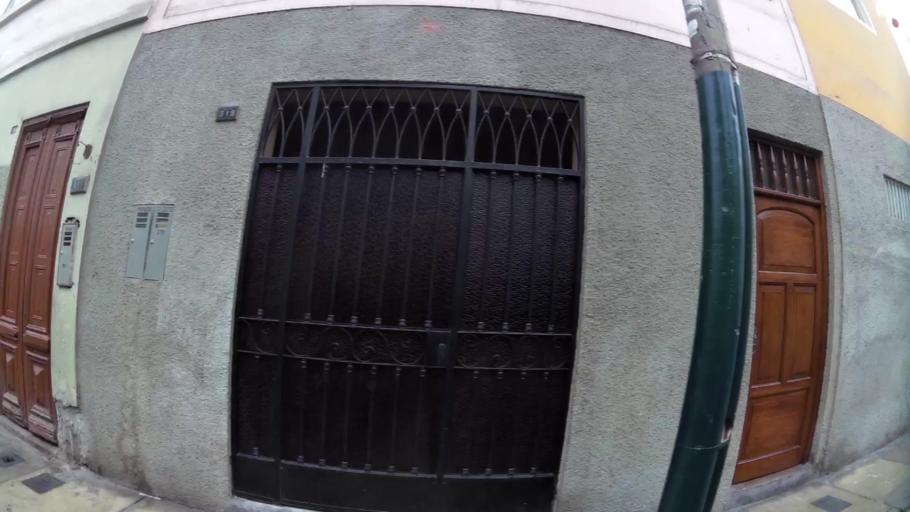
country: PE
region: Lima
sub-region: Lima
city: Surco
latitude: -12.1443
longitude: -77.0031
